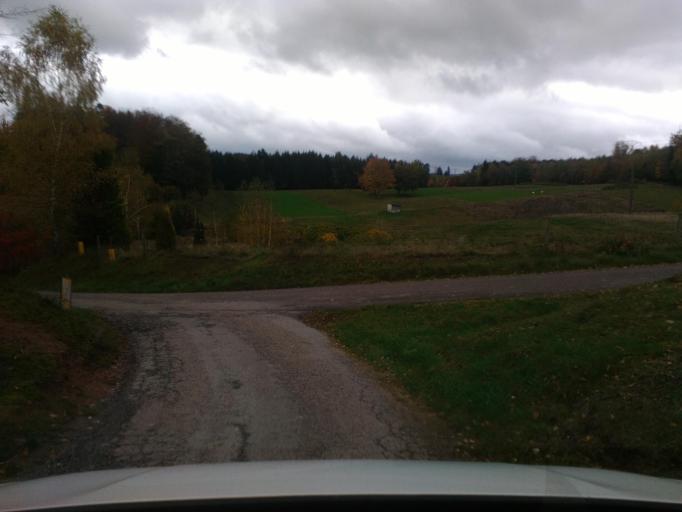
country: FR
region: Lorraine
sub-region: Departement des Vosges
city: Moyenmoutier
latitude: 48.3695
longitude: 6.8961
